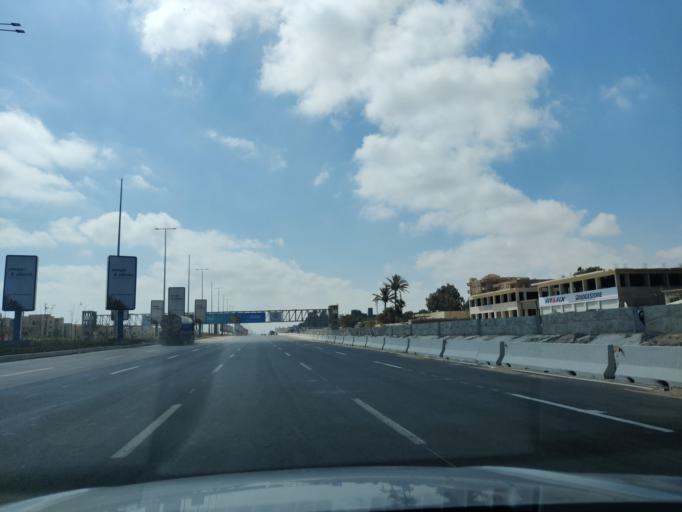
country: EG
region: Muhafazat Matruh
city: Al `Alamayn
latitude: 30.9700
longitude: 28.7405
